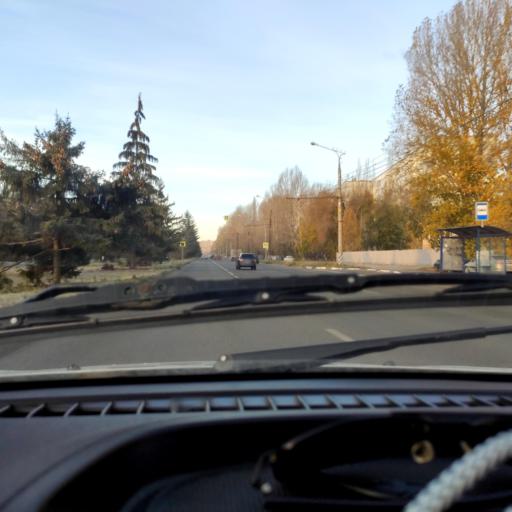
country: RU
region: Samara
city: Tol'yatti
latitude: 53.5086
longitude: 49.4525
